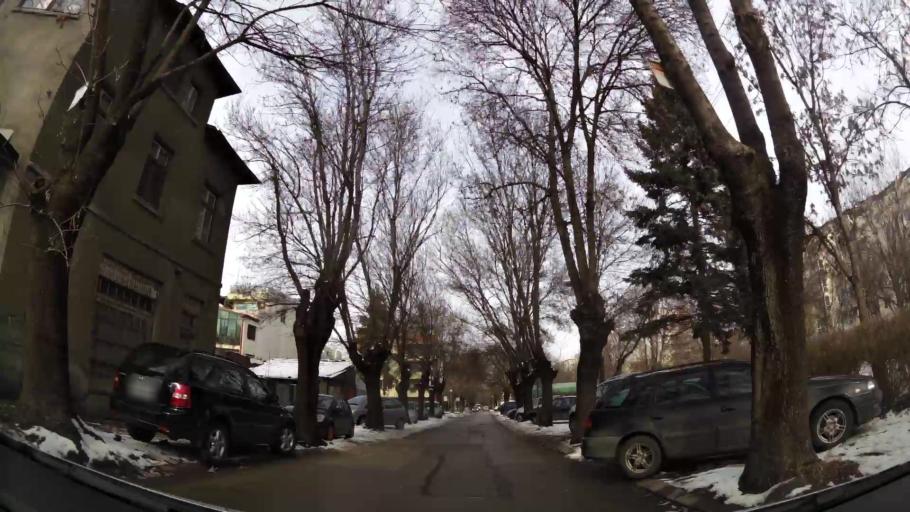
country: BG
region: Sofia-Capital
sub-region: Stolichna Obshtina
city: Sofia
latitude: 42.7025
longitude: 23.3482
